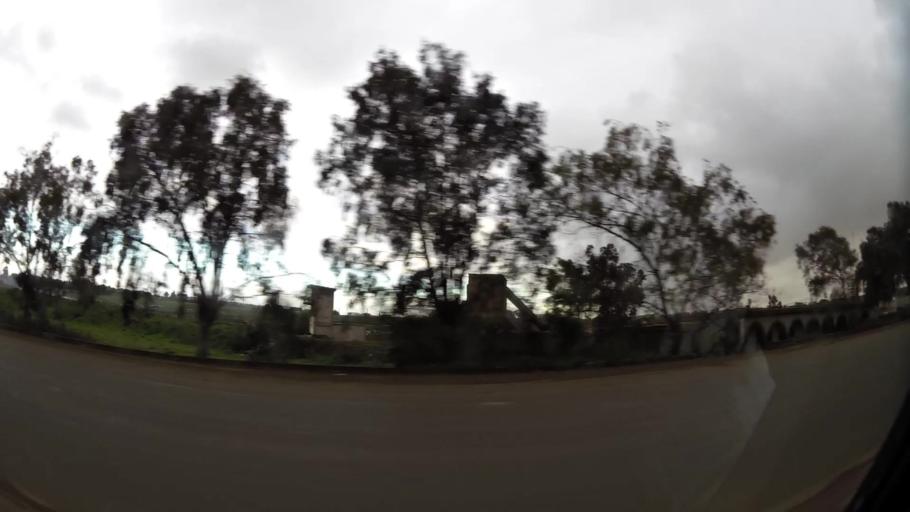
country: MA
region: Grand Casablanca
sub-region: Mediouna
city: Tit Mellil
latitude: 33.5678
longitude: -7.5124
